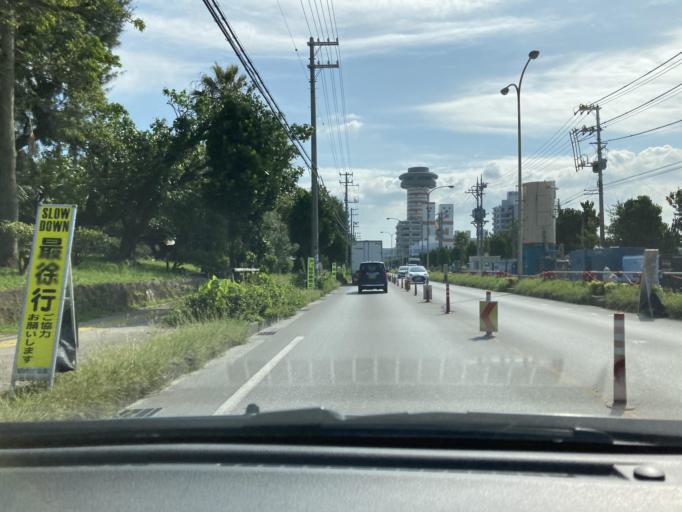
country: JP
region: Okinawa
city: Naha-shi
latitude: 26.2413
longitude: 127.6779
